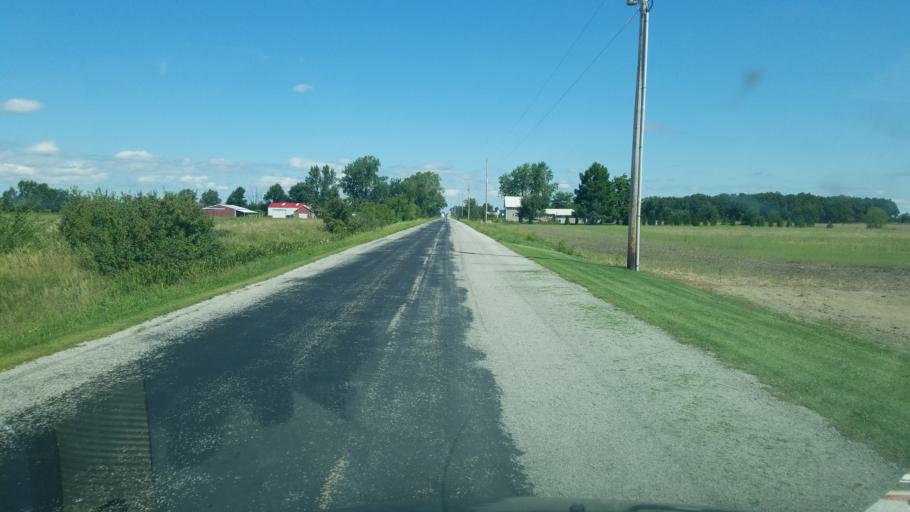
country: US
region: Ohio
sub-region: Henry County
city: Deshler
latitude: 41.2450
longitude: -83.8425
